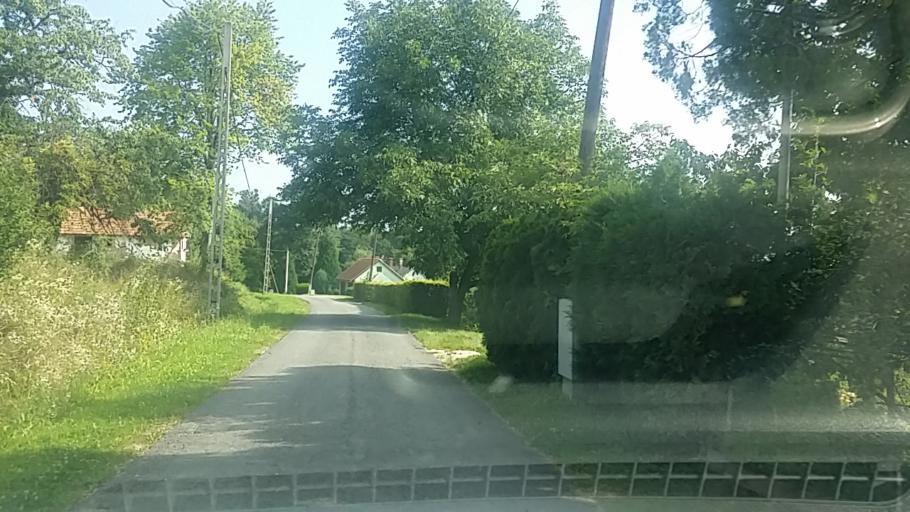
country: HU
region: Zala
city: Lenti
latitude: 46.5581
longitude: 16.5504
